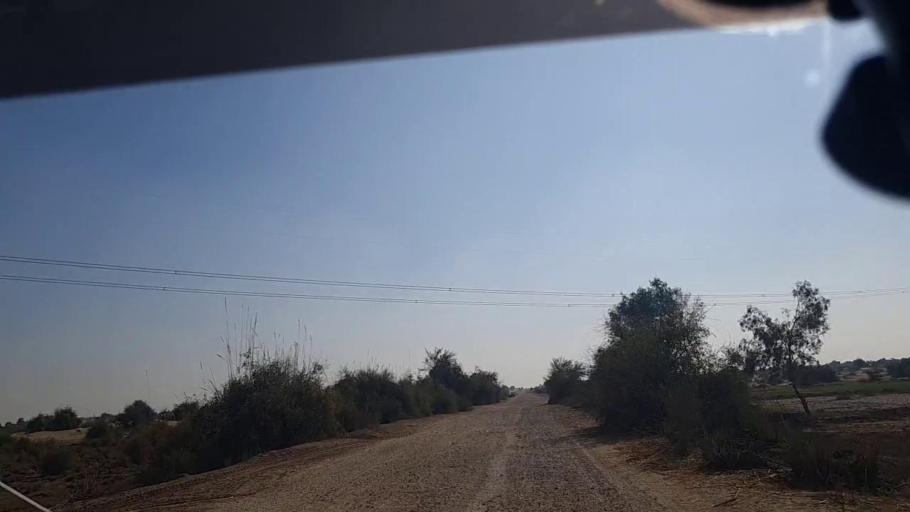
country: PK
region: Sindh
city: Khanpur
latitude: 27.5797
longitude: 69.3054
